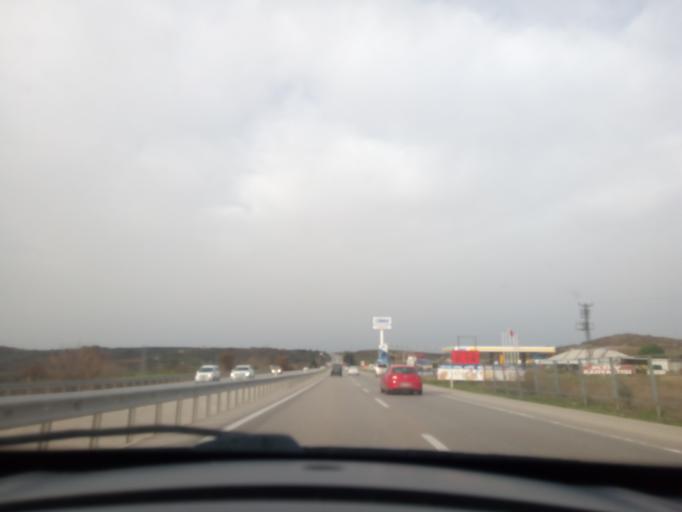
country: TR
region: Bursa
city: Mahmudiye
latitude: 40.2158
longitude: 28.6580
